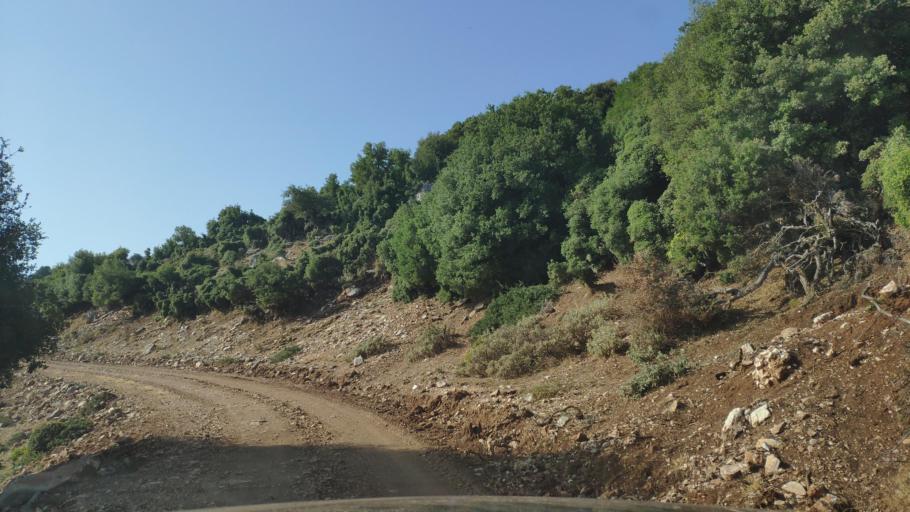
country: GR
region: West Greece
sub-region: Nomos Aitolias kai Akarnanias
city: Monastirakion
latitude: 38.8332
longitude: 20.9718
